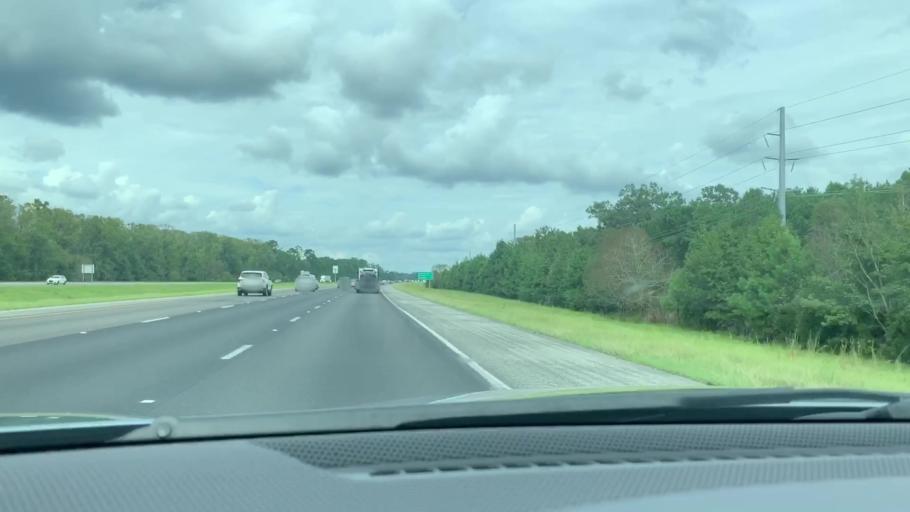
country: US
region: Georgia
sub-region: Liberty County
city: Midway
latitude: 31.7908
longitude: -81.3751
